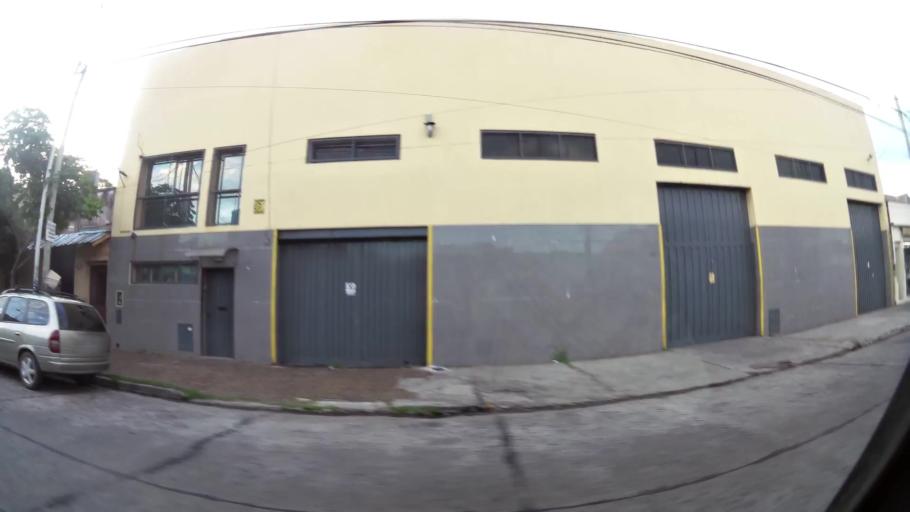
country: AR
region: Buenos Aires
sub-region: Partido de Avellaneda
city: Avellaneda
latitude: -34.7002
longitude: -58.3300
